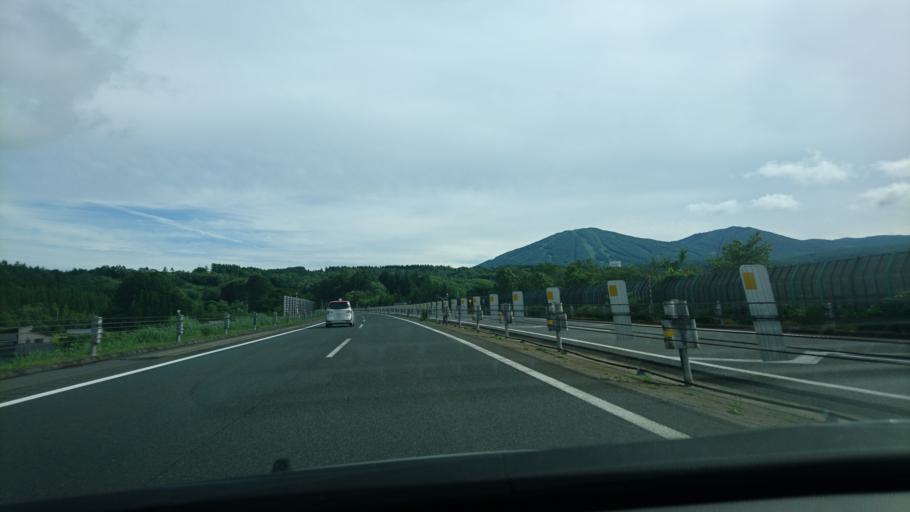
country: JP
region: Akita
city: Hanawa
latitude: 40.0263
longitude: 140.9828
